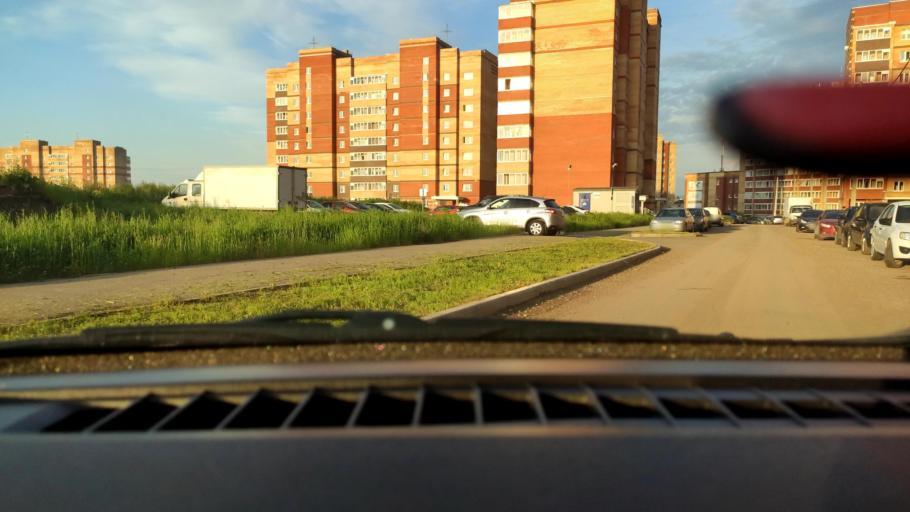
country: RU
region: Perm
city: Froly
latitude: 57.9243
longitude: 56.2757
